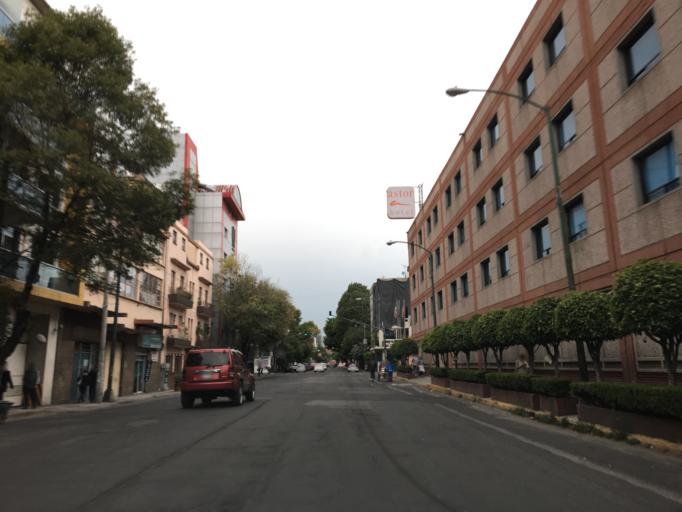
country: MX
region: Mexico City
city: Cuauhtemoc
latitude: 19.4346
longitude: -99.1597
